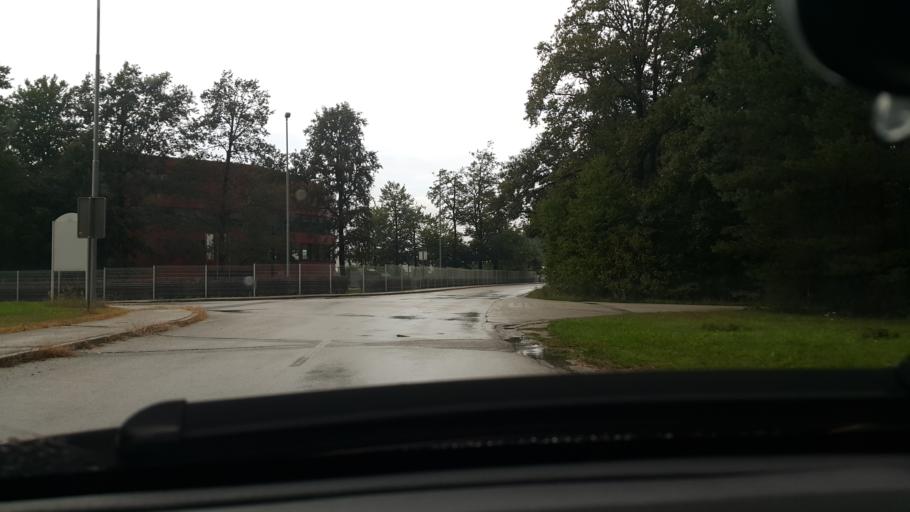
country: SI
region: Hoce-Slivnica
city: Rogoza
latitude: 46.5221
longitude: 15.6717
